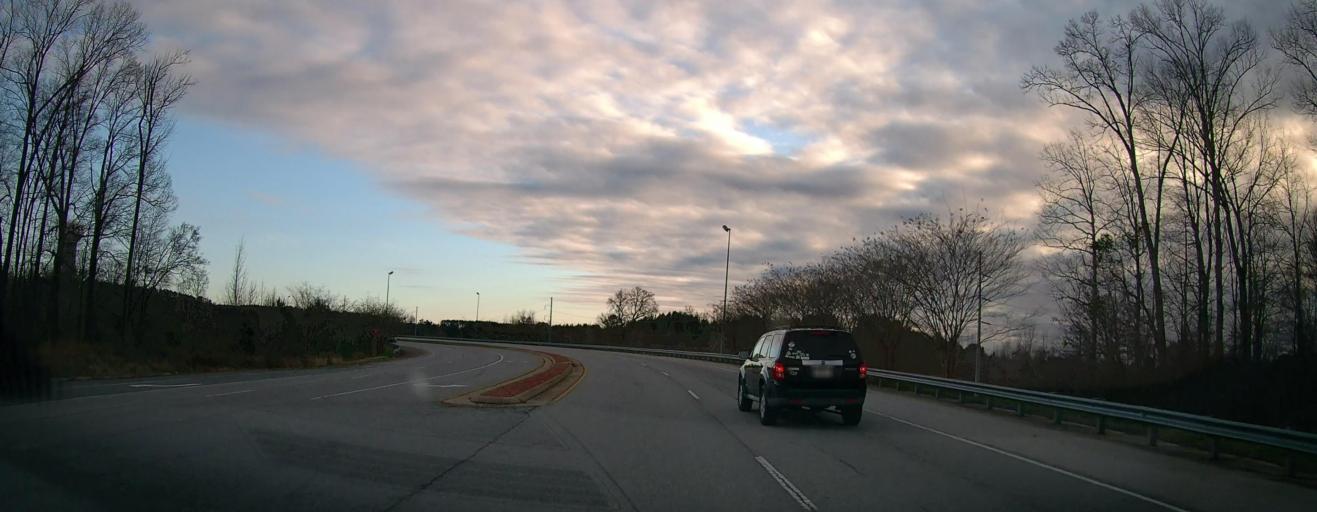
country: US
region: Georgia
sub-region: Troup County
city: West Point
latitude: 32.9276
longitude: -85.1159
